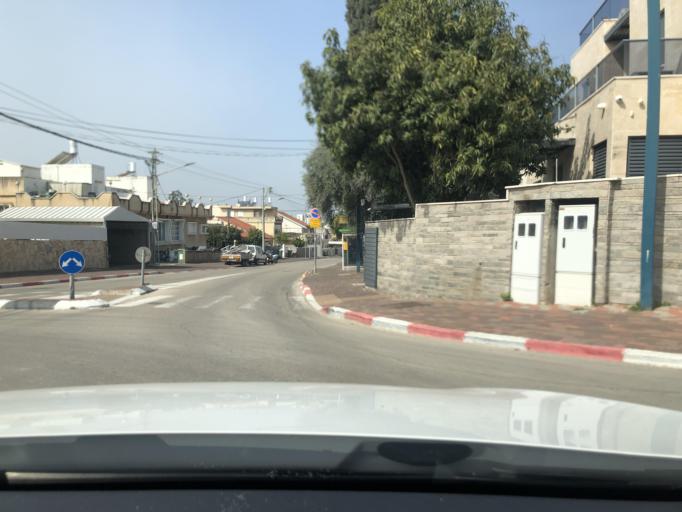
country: IL
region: Central District
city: Rosh Ha'Ayin
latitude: 32.0929
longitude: 34.9520
